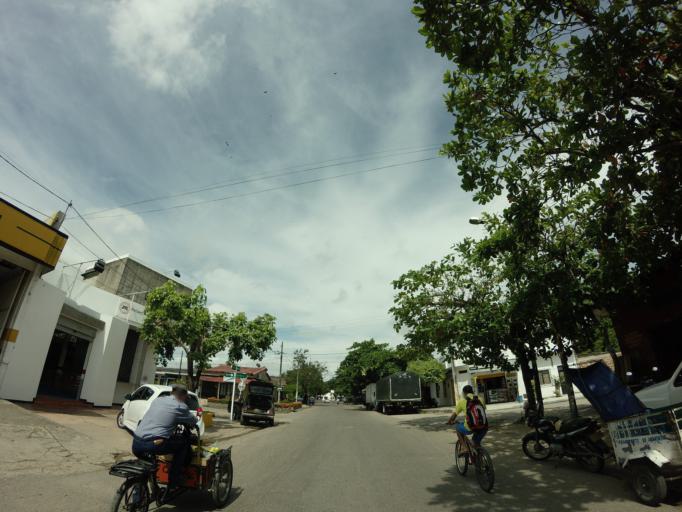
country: CO
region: Caldas
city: La Dorada
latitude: 5.4479
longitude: -74.6686
